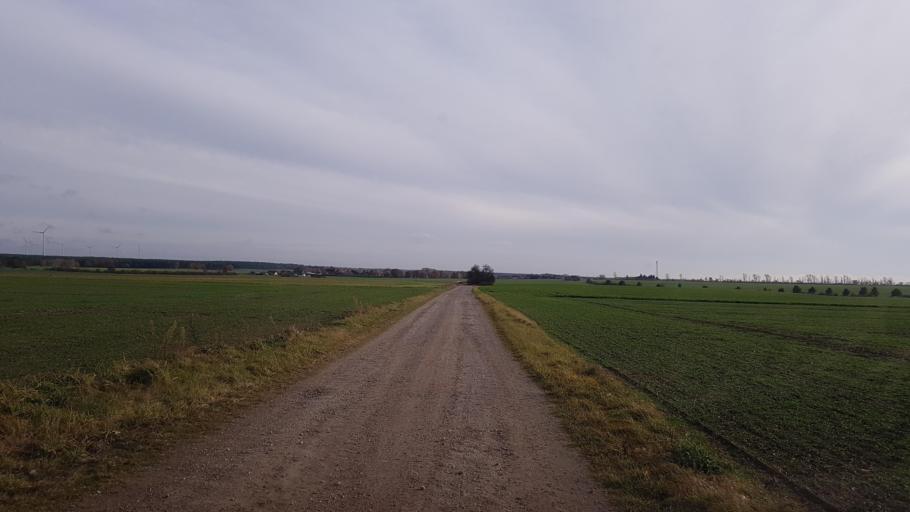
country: DE
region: Brandenburg
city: Treuenbrietzen
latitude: 52.0151
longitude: 12.9010
